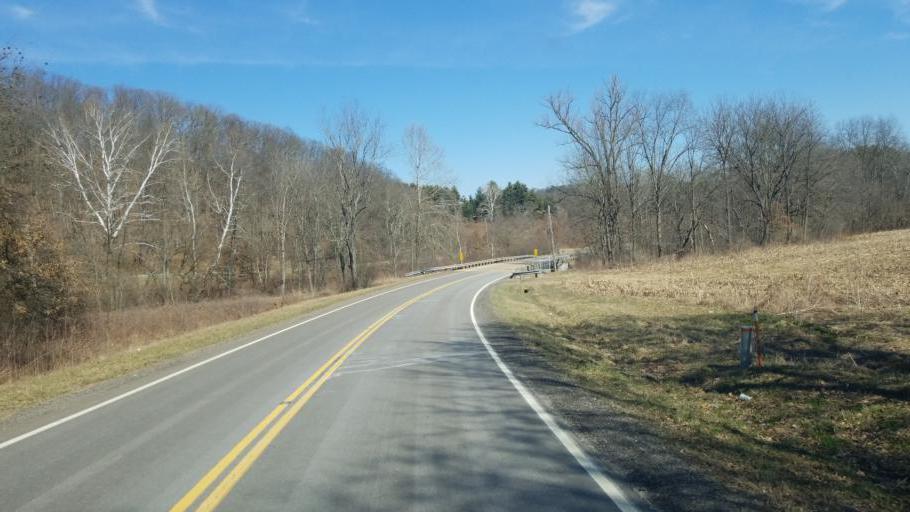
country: US
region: Ohio
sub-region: Knox County
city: Danville
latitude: 40.5155
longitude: -82.2105
